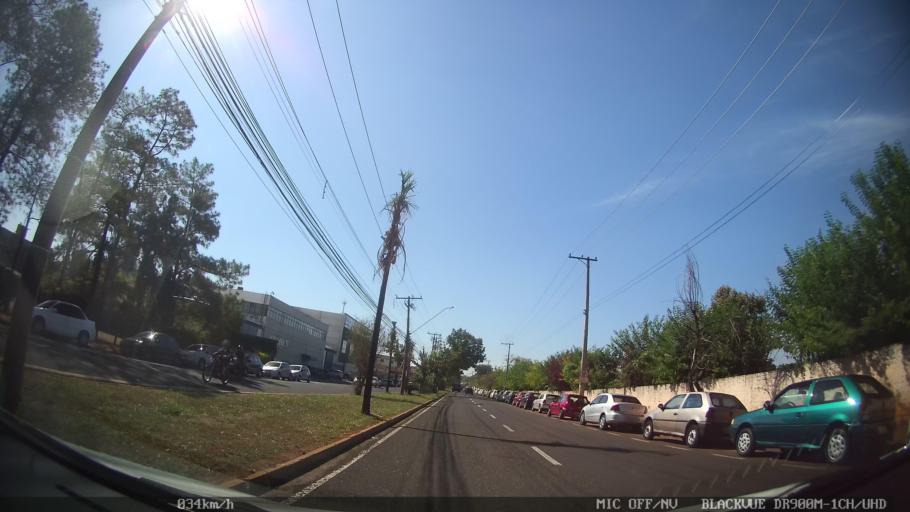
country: BR
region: Sao Paulo
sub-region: Sao Jose Do Rio Preto
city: Sao Jose do Rio Preto
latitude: -20.8101
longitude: -49.4098
